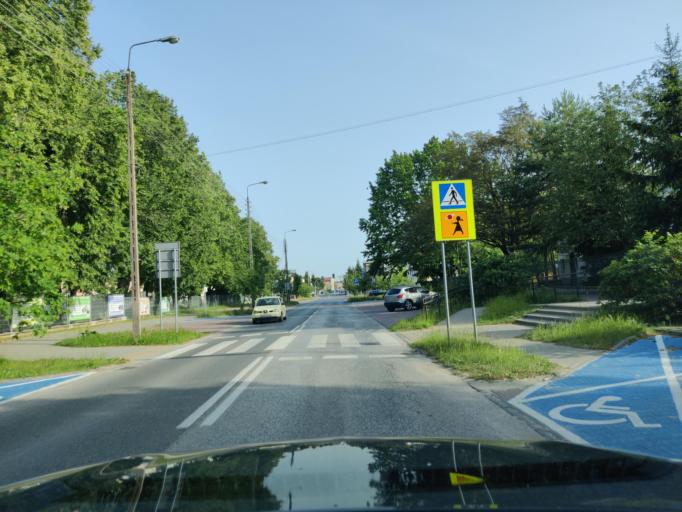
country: PL
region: Masovian Voivodeship
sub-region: Powiat wyszkowski
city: Wyszkow
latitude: 52.6018
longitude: 21.4556
